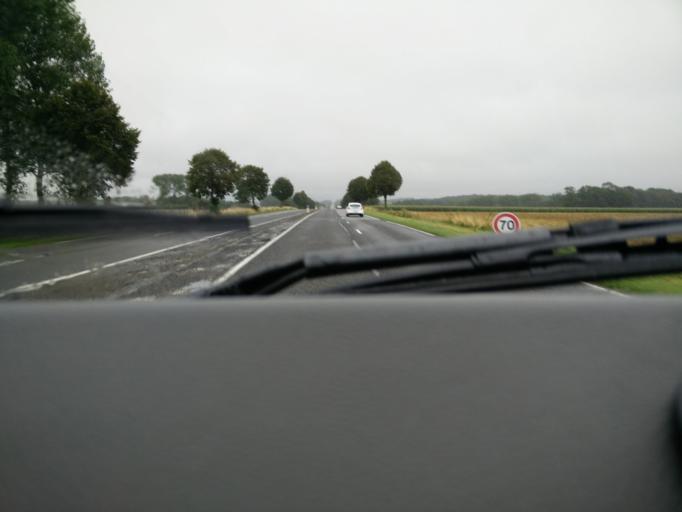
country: FR
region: Nord-Pas-de-Calais
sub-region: Departement du Pas-de-Calais
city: Auchy-les-Hesdin
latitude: 50.3847
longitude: 2.1515
